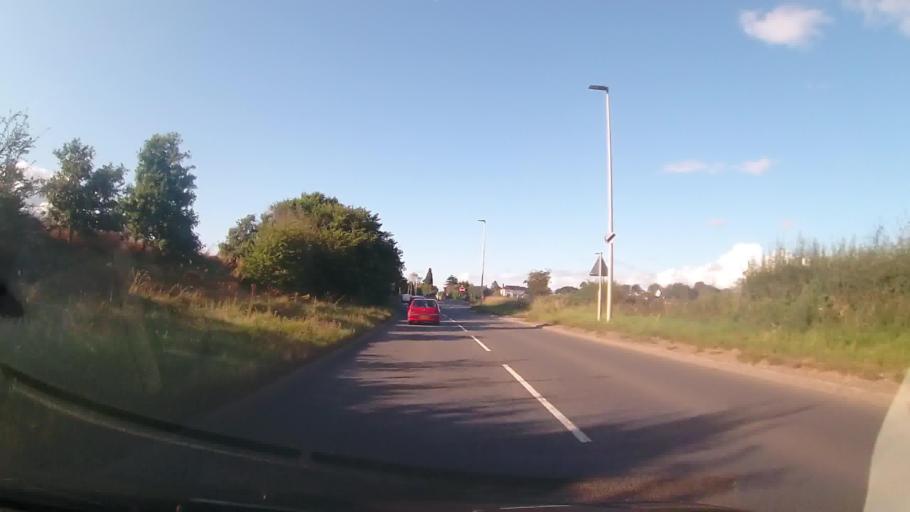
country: GB
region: England
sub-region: Shropshire
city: Bayston Hill
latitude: 52.6698
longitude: -2.7612
